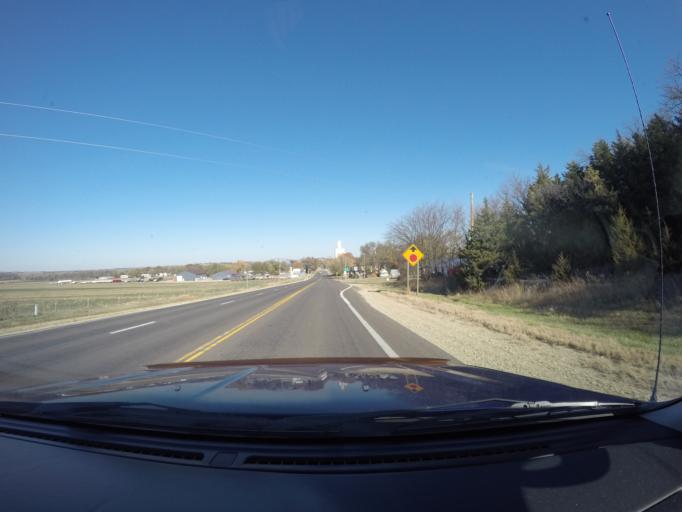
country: US
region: Kansas
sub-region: Marshall County
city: Blue Rapids
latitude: 39.6858
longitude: -96.7510
